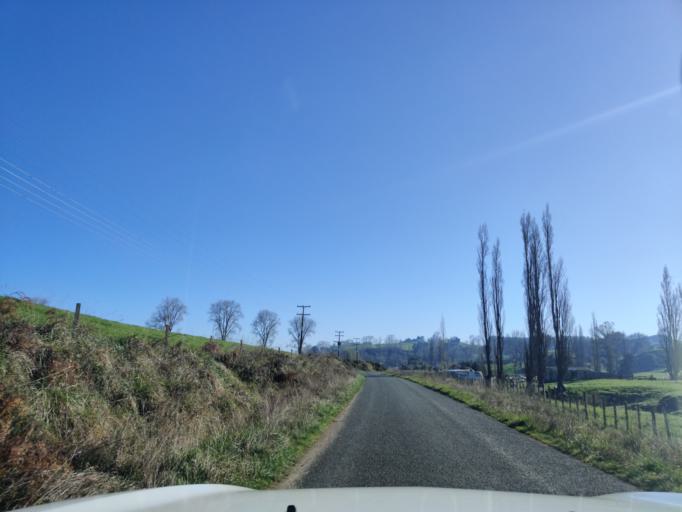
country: NZ
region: Waikato
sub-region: Matamata-Piako District
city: Matamata
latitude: -37.9920
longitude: 175.7166
